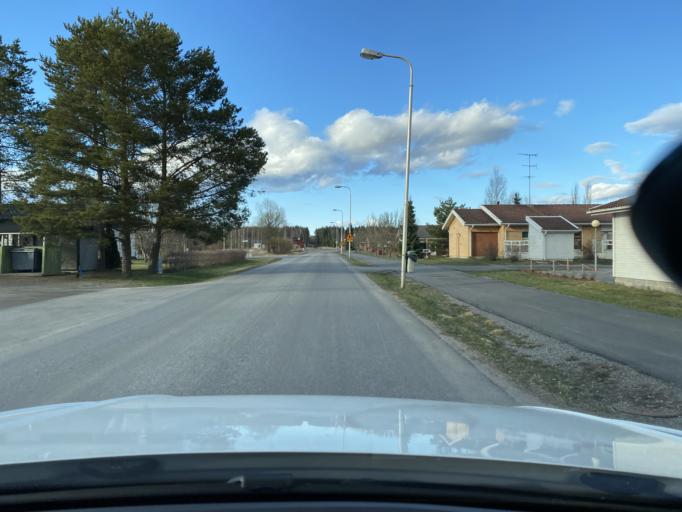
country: FI
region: Pirkanmaa
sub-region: Lounais-Pirkanmaa
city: Punkalaidun
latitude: 61.1163
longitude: 23.1110
